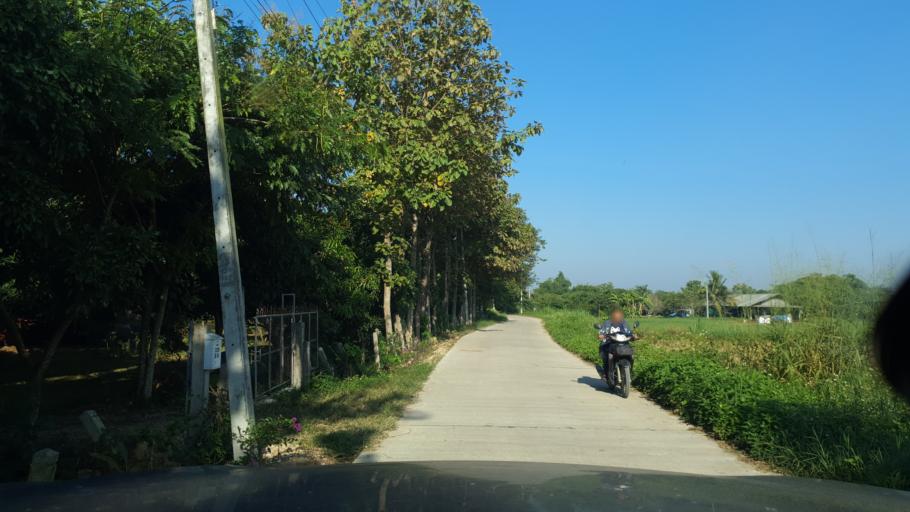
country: TH
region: Chiang Mai
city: San Kamphaeng
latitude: 18.6878
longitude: 99.1509
